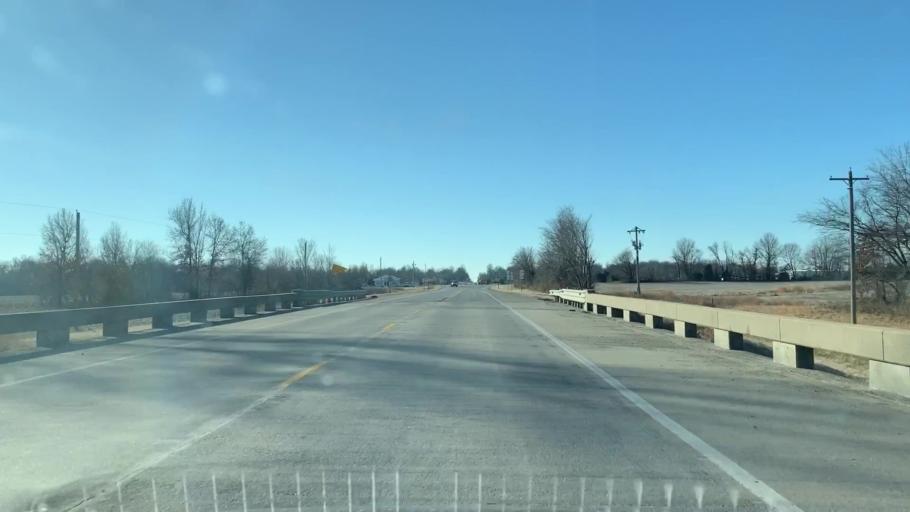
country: US
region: Kansas
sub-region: Cherokee County
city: Galena
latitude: 37.1827
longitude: -94.7046
